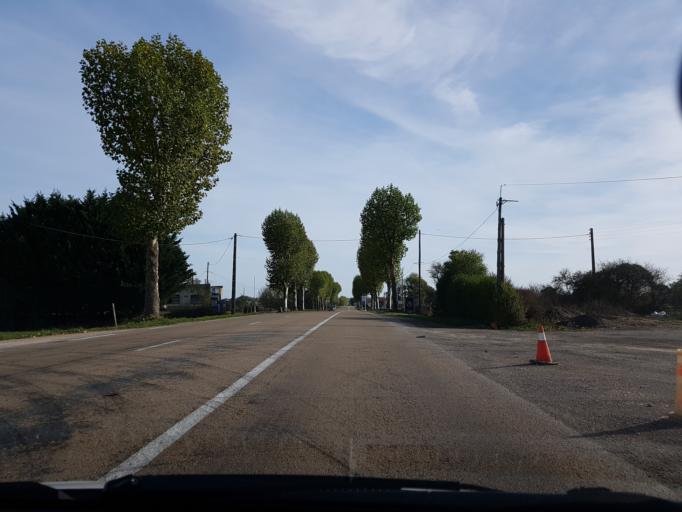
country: FR
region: Bourgogne
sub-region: Departement de l'Yonne
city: Avallon
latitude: 47.4782
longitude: 4.0092
